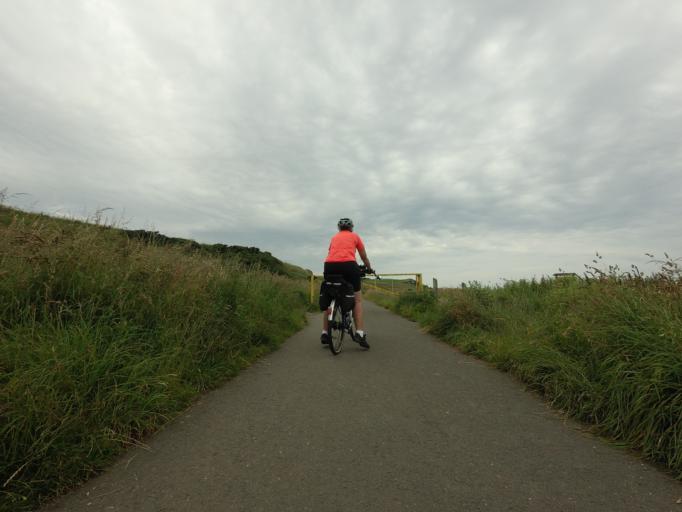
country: GB
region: Scotland
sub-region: Aberdeenshire
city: Whitehills
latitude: 57.6758
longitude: -2.5681
